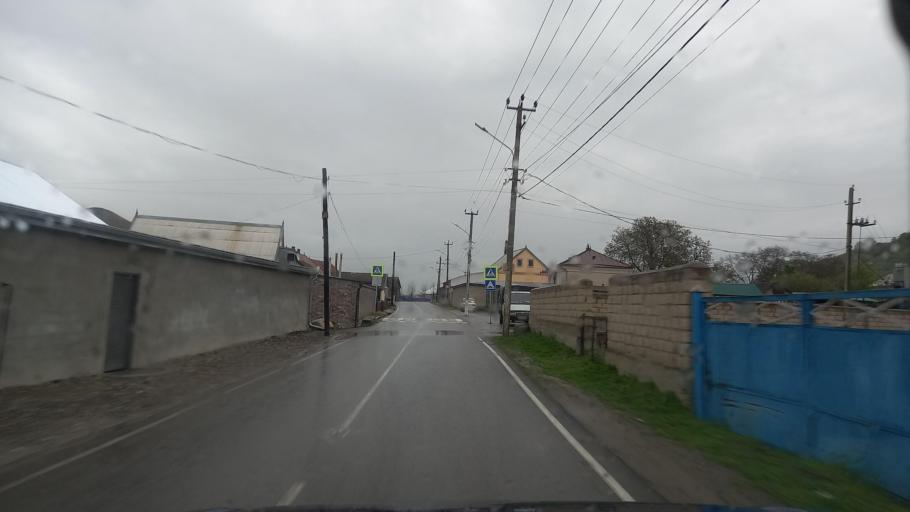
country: RU
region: Kabardino-Balkariya
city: Gundelen
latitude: 43.5952
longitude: 43.1726
